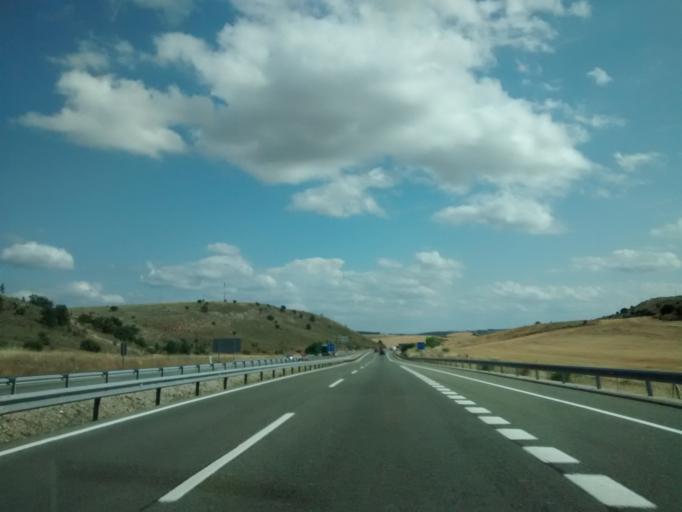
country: ES
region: Castille-La Mancha
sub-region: Provincia de Guadalajara
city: Alcolea del Pinar
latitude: 41.0903
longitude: -2.4468
